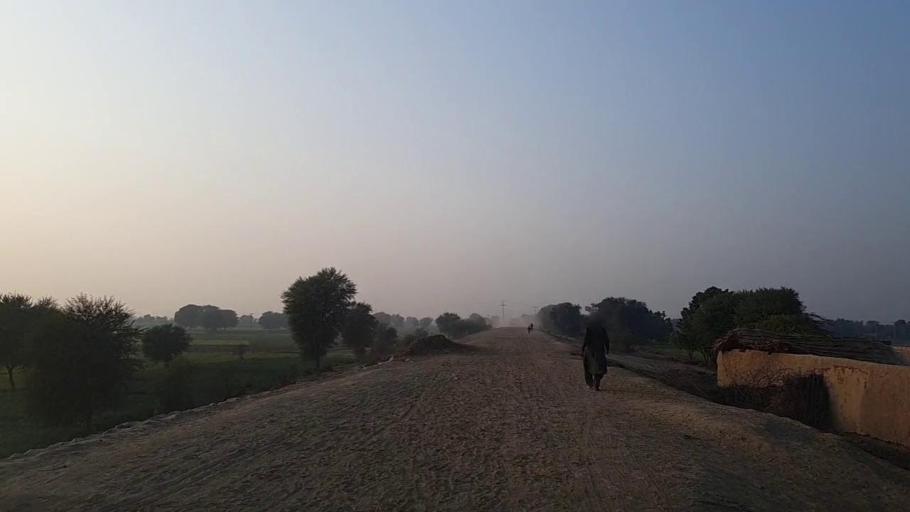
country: PK
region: Sindh
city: Sann
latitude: 26.1731
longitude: 68.1025
